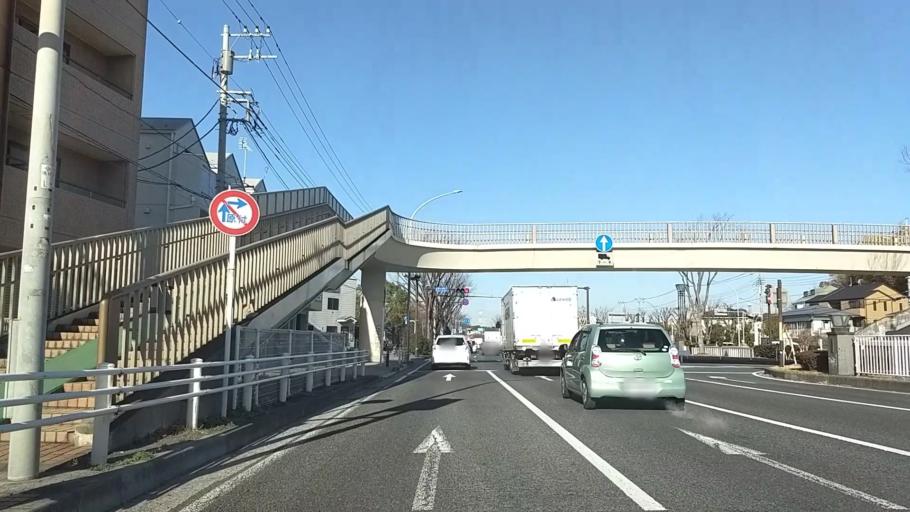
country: JP
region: Kanagawa
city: Yokohama
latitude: 35.4050
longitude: 139.5690
